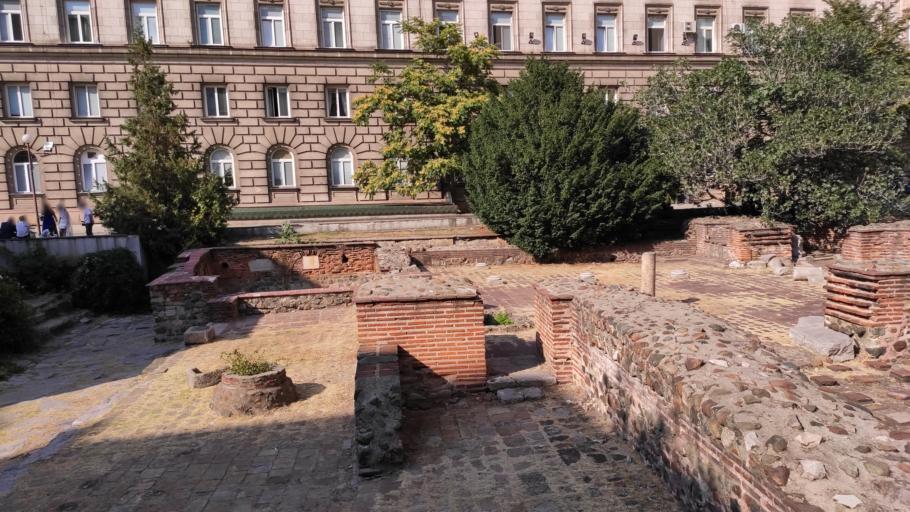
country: BG
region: Sofia-Capital
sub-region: Stolichna Obshtina
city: Sofia
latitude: 42.6967
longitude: 23.3231
